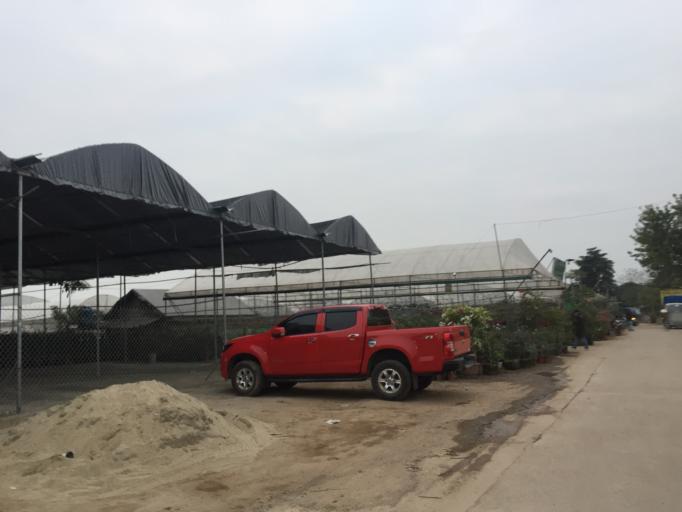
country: VN
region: Hung Yen
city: Van Giang
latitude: 20.9689
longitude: 105.9176
